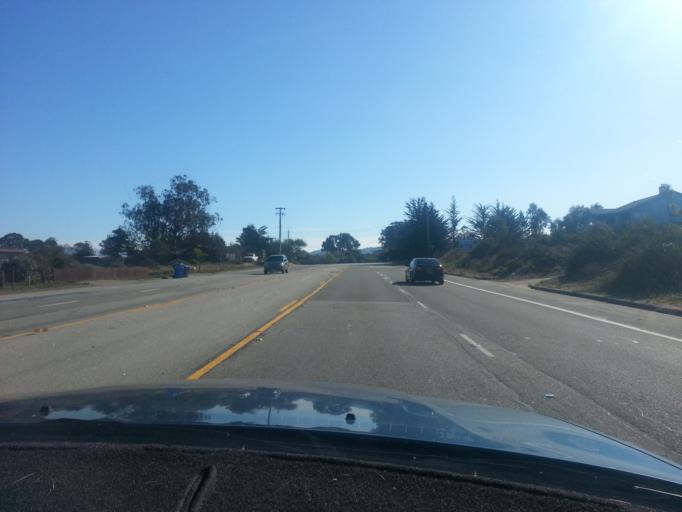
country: US
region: California
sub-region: San Luis Obispo County
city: Los Osos
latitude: 35.3096
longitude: -120.8248
